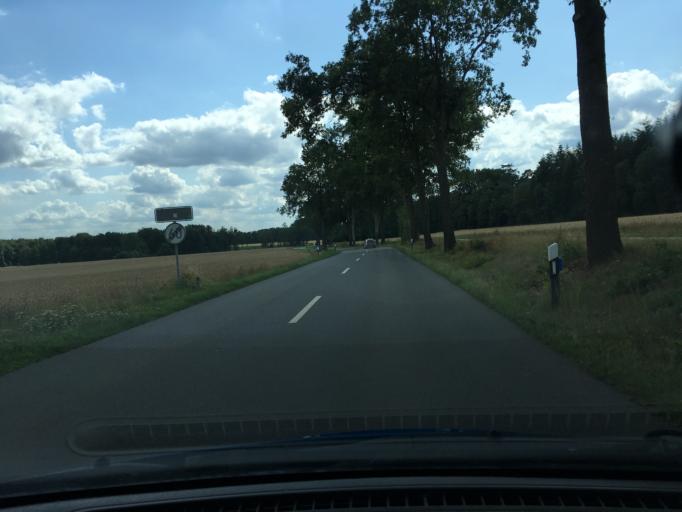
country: DE
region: Lower Saxony
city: Bienenbuttel
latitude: 53.1584
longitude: 10.4964
